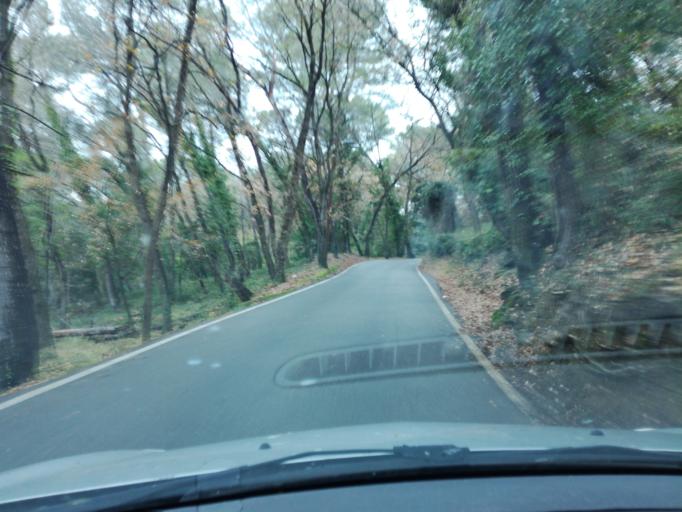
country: FR
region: Provence-Alpes-Cote d'Azur
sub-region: Departement des Alpes-Maritimes
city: Mouans-Sartoux
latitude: 43.6056
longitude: 6.9817
